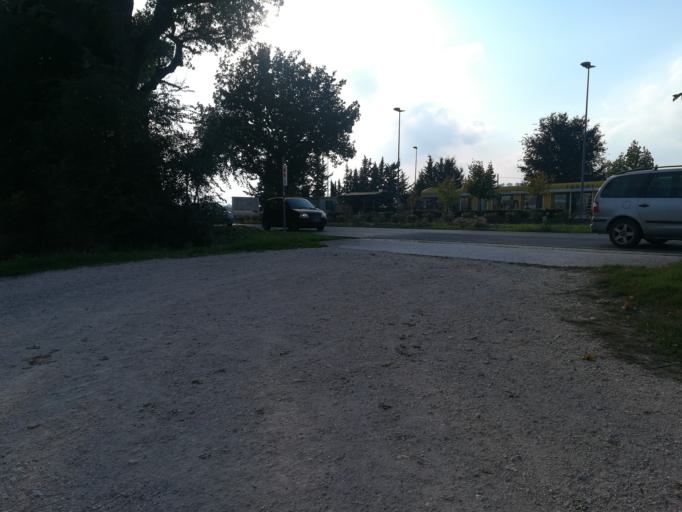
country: IT
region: The Marches
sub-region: Provincia di Macerata
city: Sforzacosta
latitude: 43.2705
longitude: 13.4257
